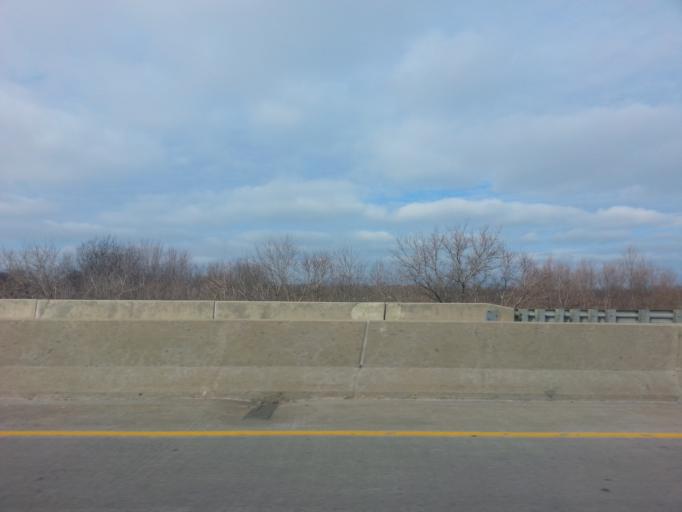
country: US
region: Illinois
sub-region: Winnebago County
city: Cherry Valley
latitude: 42.2233
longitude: -88.9837
